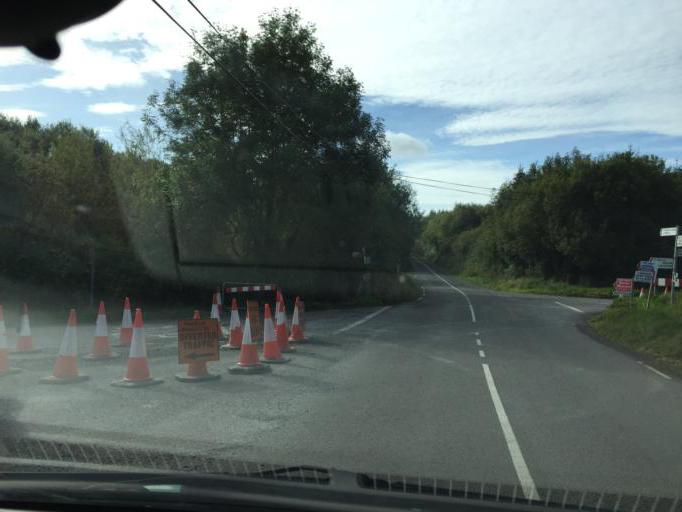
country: IE
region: Connaught
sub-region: Roscommon
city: Boyle
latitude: 54.0288
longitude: -8.2811
